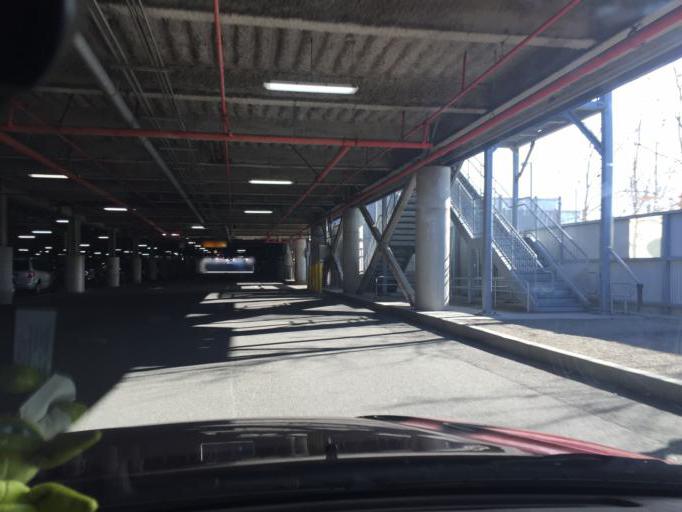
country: US
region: New York
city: New York City
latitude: 40.6711
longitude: -74.0120
